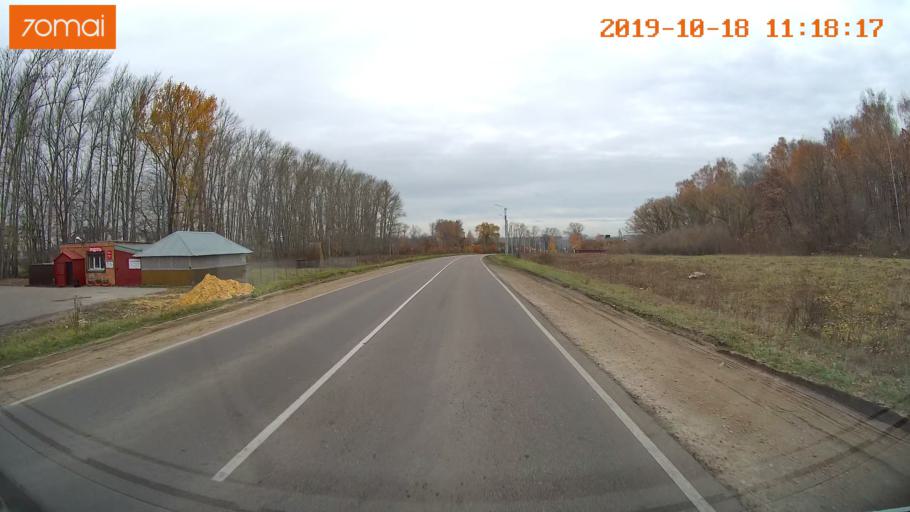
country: RU
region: Tula
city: Kimovsk
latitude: 54.0374
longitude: 38.5503
